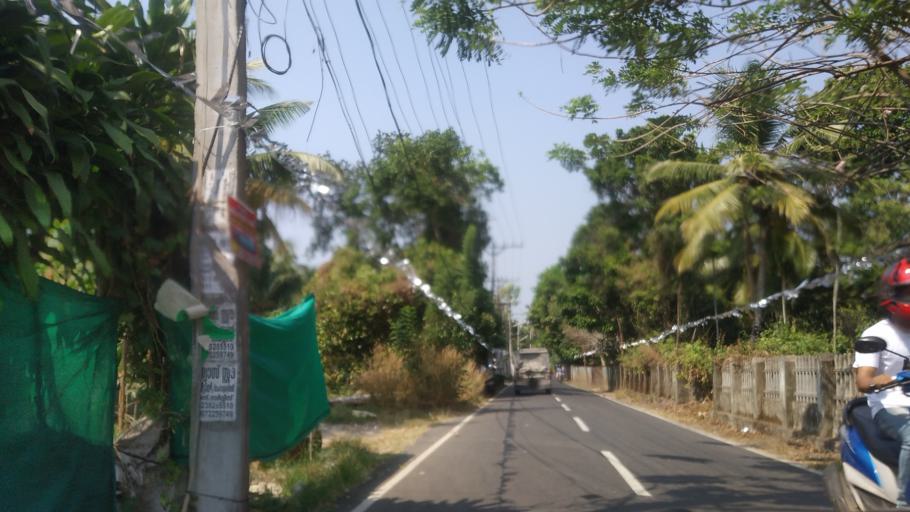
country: IN
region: Kerala
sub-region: Ernakulam
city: Elur
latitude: 10.1277
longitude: 76.2363
